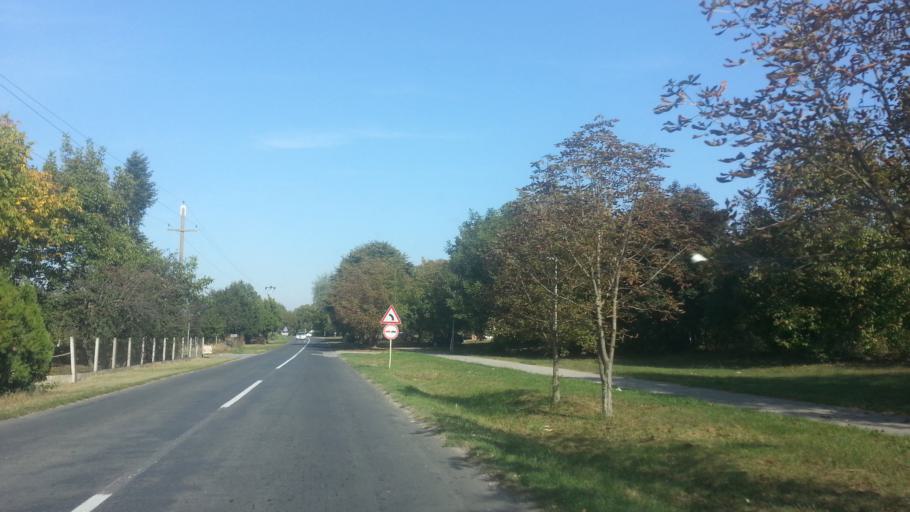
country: RS
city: Belegis
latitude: 45.0054
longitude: 20.3105
